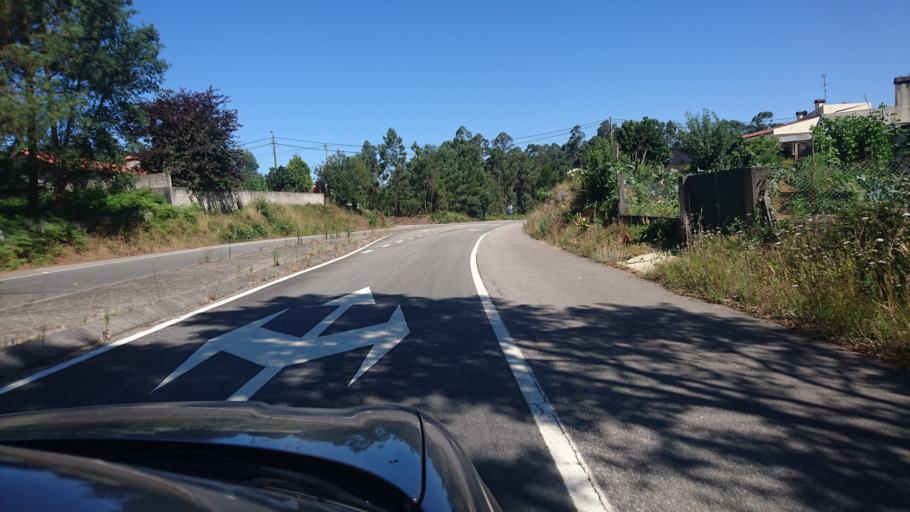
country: PT
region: Aveiro
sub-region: Santa Maria da Feira
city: Rio Meao
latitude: 40.9462
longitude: -8.5874
